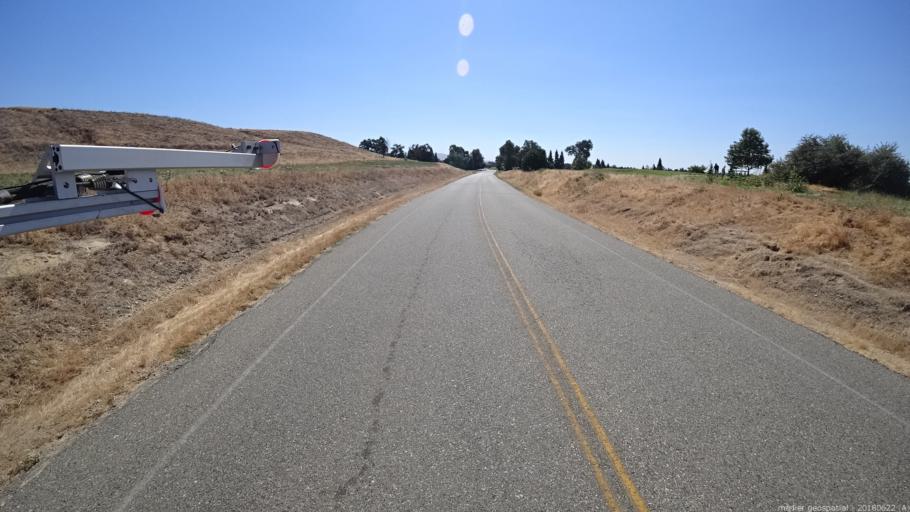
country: US
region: California
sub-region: Fresno County
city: Clovis
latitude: 36.9277
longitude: -119.7636
